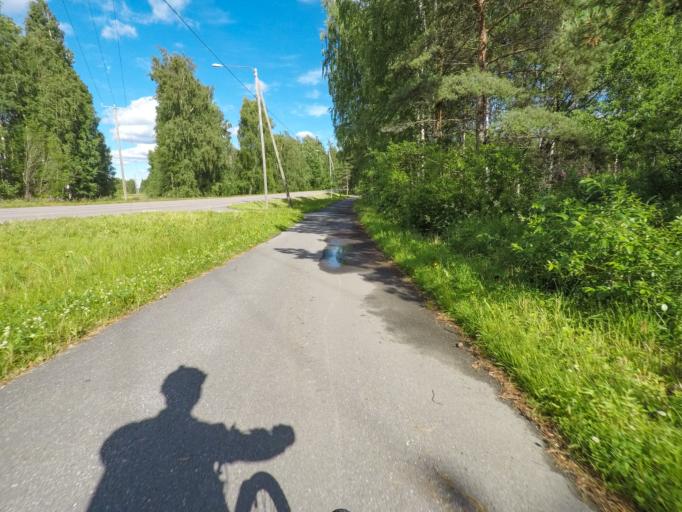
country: FI
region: South Karelia
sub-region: Lappeenranta
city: Joutseno
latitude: 61.1285
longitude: 28.5102
